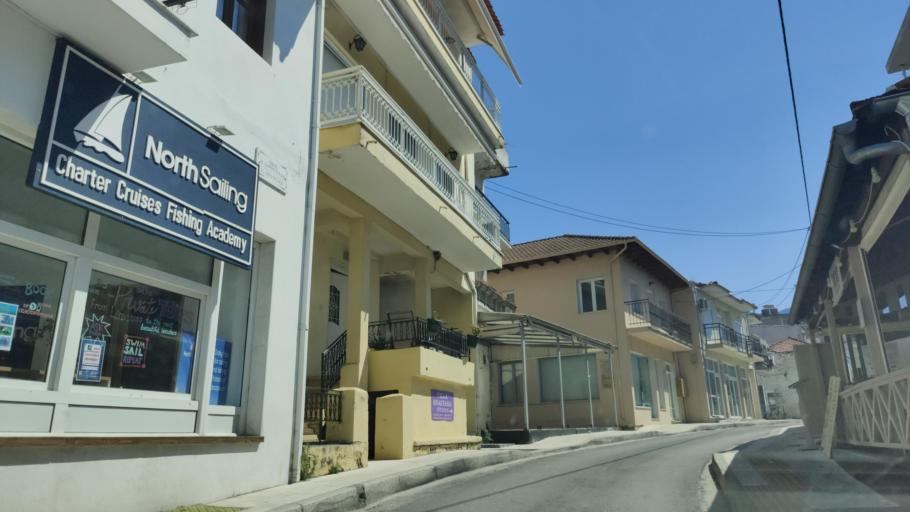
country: GR
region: East Macedonia and Thrace
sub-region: Nomos Kavalas
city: Thasos
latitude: 40.7787
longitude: 24.7080
